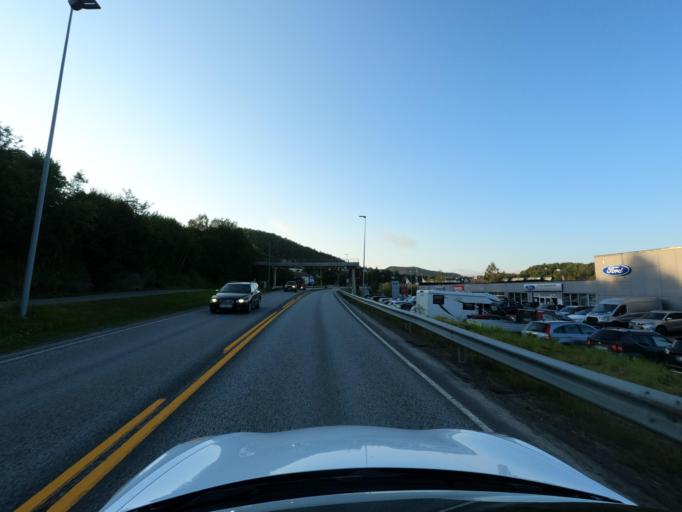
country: NO
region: Troms
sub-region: Harstad
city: Harstad
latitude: 68.7704
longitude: 16.5578
